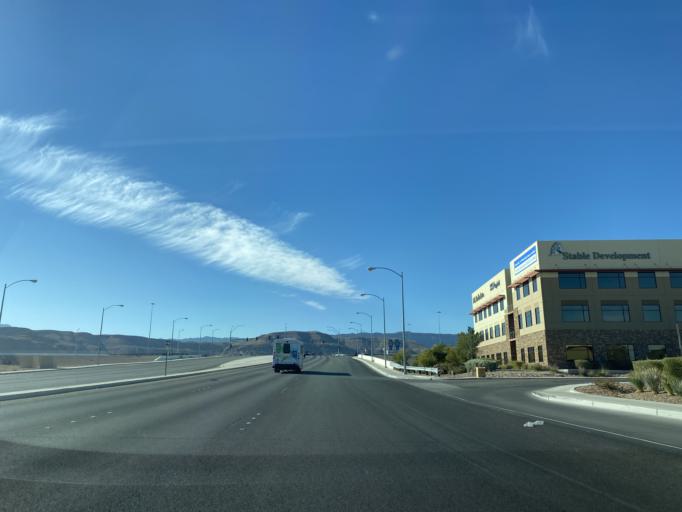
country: US
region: Nevada
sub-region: Clark County
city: Spring Valley
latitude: 36.0704
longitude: -115.2845
